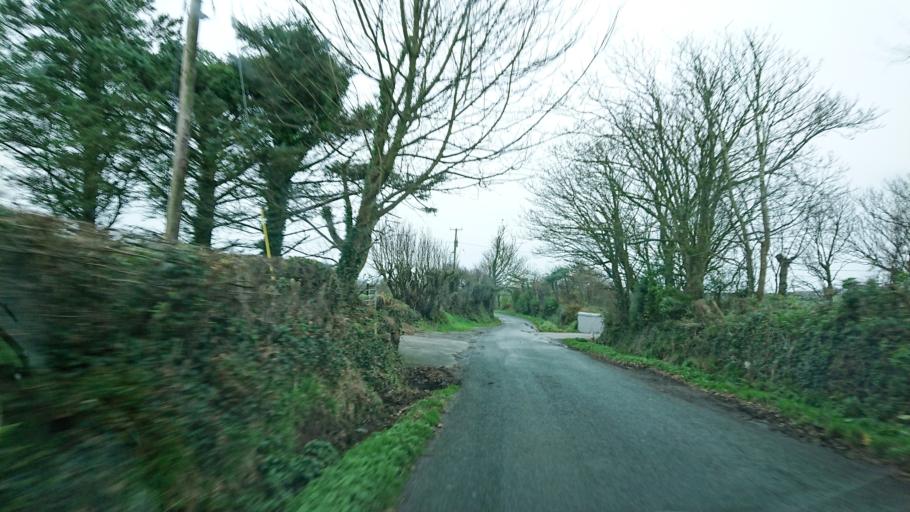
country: IE
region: Munster
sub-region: Waterford
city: Dunmore East
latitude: 52.1497
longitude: -7.0584
